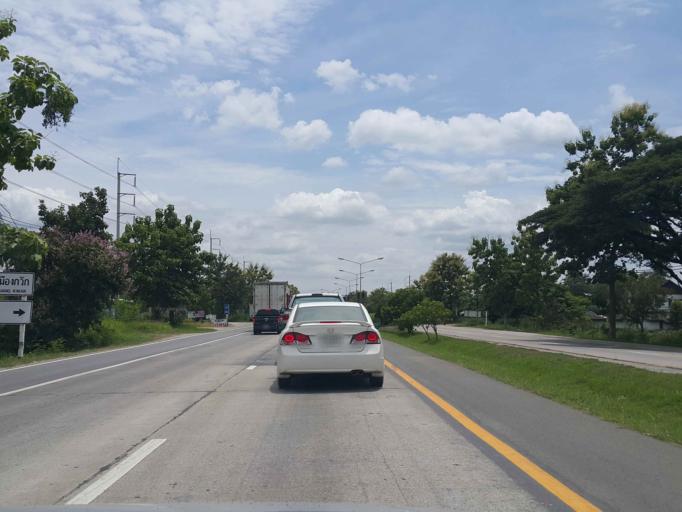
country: TH
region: Lamphun
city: Ban Thi
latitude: 18.6359
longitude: 99.0515
